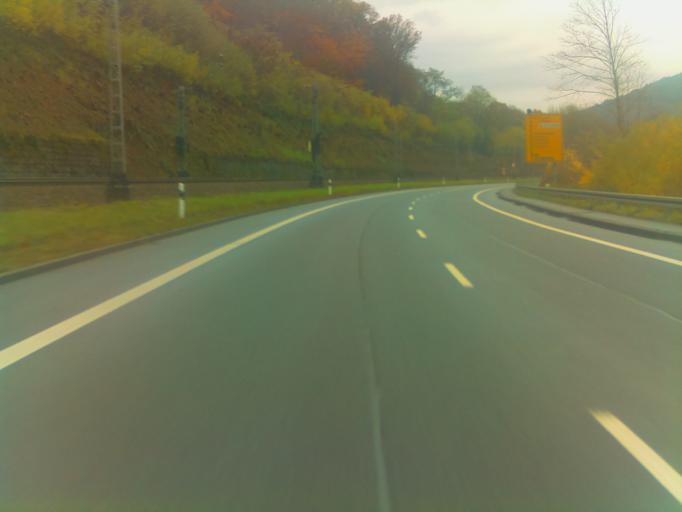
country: DE
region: Hesse
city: Hirschhorn
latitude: 49.4303
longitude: 8.8927
